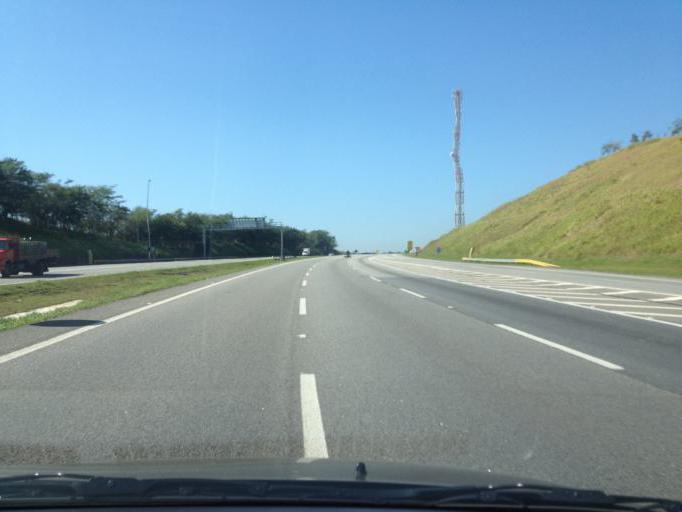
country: BR
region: Sao Paulo
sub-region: Jacarei
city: Jacarei
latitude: -23.3444
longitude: -46.0133
